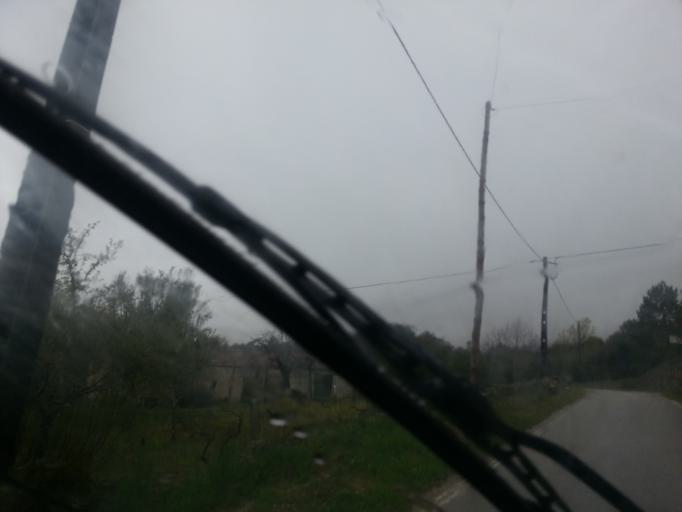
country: PT
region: Guarda
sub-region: Fornos de Algodres
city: Fornos de Algodres
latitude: 40.6199
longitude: -7.5231
